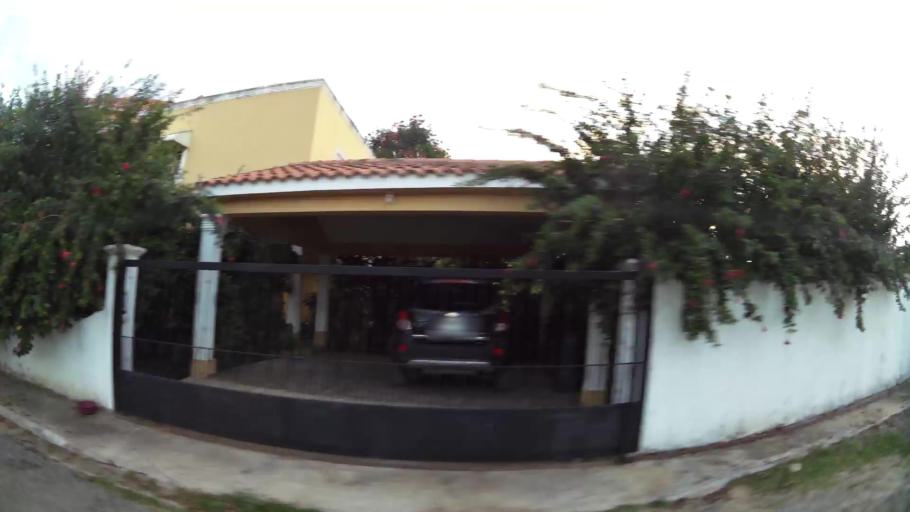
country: DO
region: Nacional
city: La Agustina
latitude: 18.5661
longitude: -69.9421
